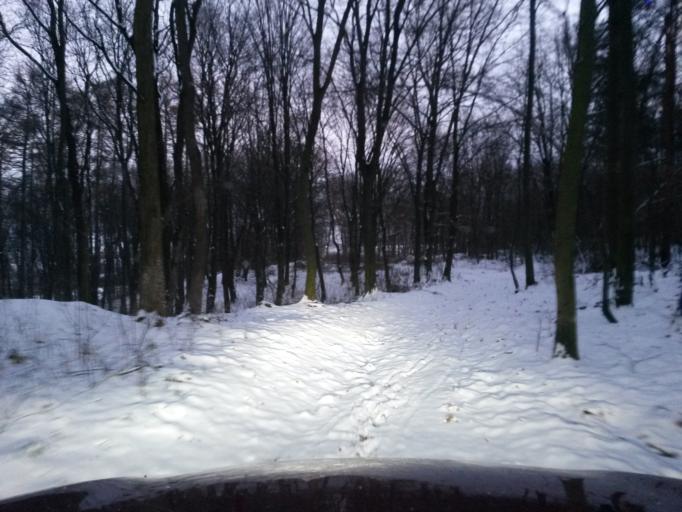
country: SK
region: Kosicky
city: Kosice
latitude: 48.7350
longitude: 21.3230
